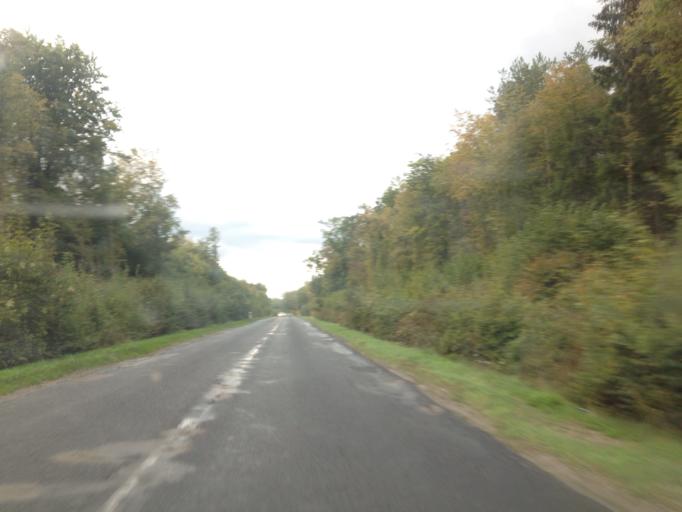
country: PL
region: Pomeranian Voivodeship
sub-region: Powiat kwidzynski
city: Prabuty
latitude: 53.7484
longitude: 19.1525
